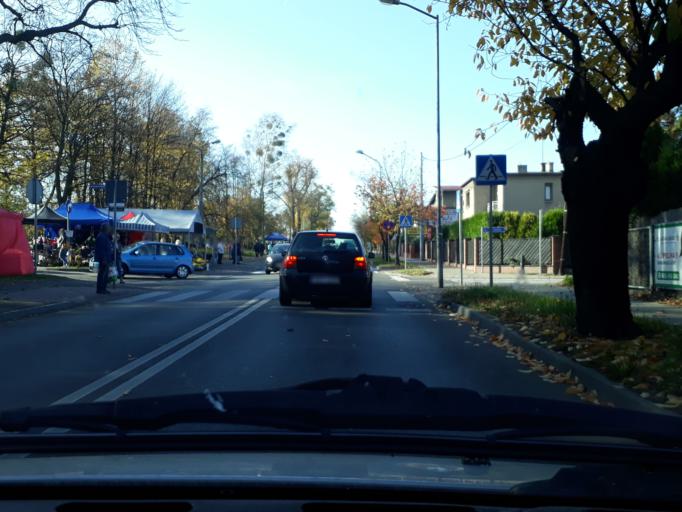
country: PL
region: Silesian Voivodeship
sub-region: Powiat tarnogorski
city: Tarnowskie Gory
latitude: 50.4423
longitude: 18.8403
